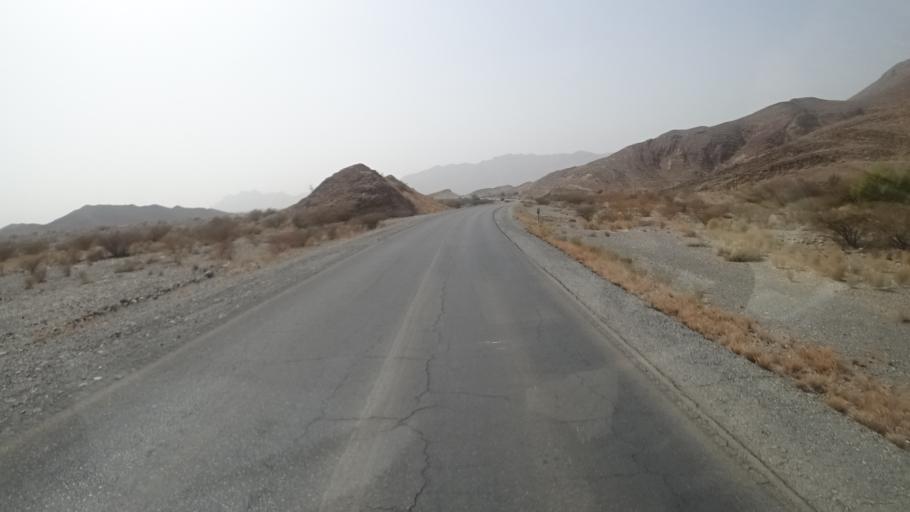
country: OM
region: Muhafazat ad Dakhiliyah
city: Nizwa
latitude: 22.9244
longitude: 57.6461
